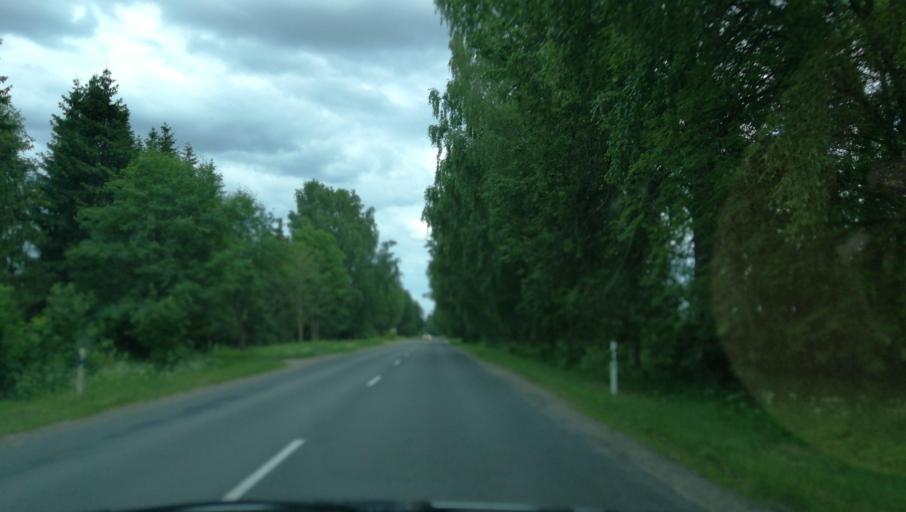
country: LV
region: Rujienas
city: Rujiena
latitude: 57.8794
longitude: 25.3581
